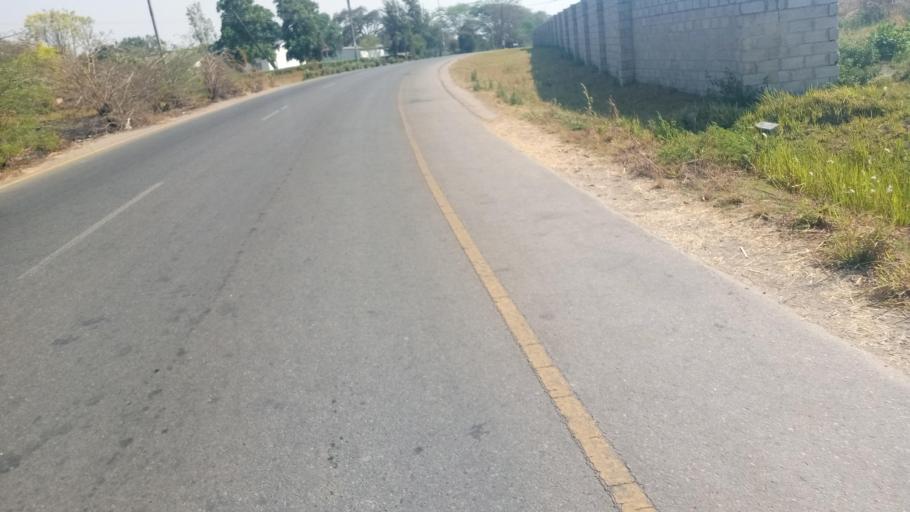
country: ZM
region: Lusaka
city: Lusaka
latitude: -15.4563
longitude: 28.4341
